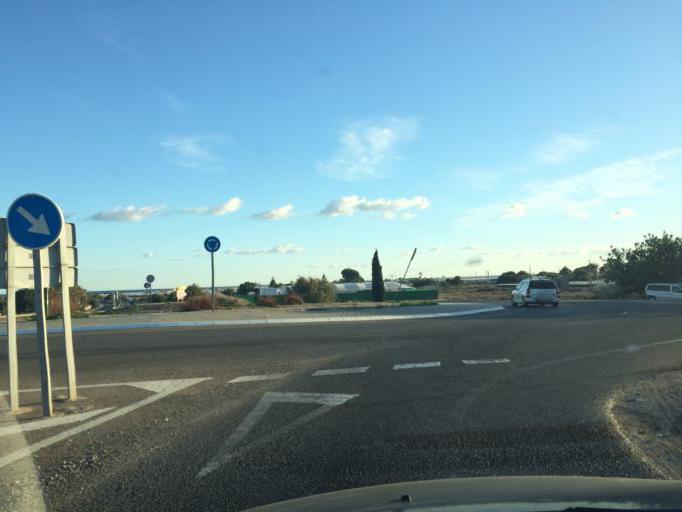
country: ES
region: Andalusia
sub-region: Provincia de Almeria
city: Almeria
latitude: 36.8342
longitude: -2.4162
